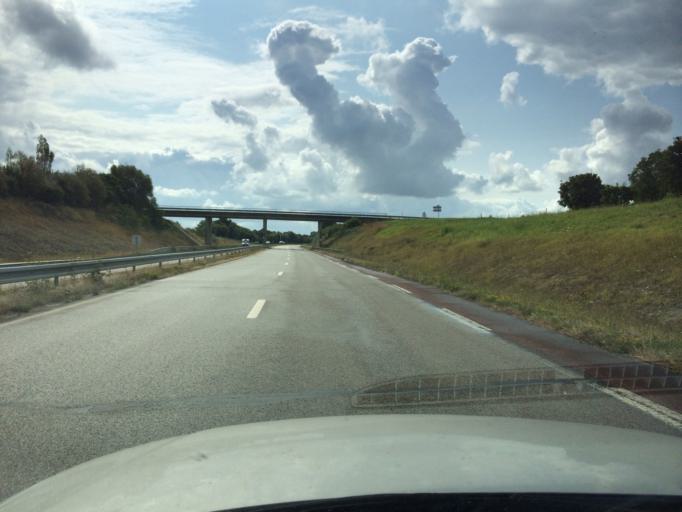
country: FR
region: Lower Normandy
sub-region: Departement de la Manche
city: Montebourg
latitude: 49.4658
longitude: -1.3615
